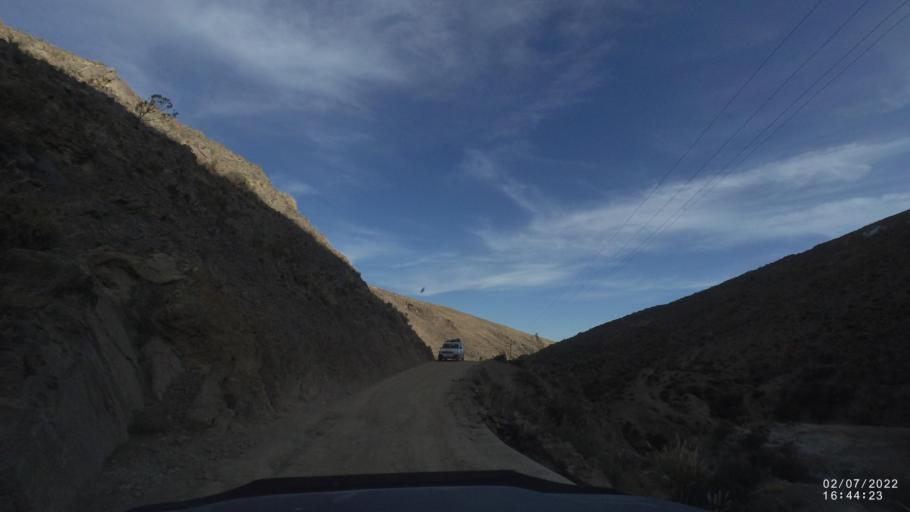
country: BO
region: Cochabamba
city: Irpa Irpa
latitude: -17.9728
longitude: -66.5098
